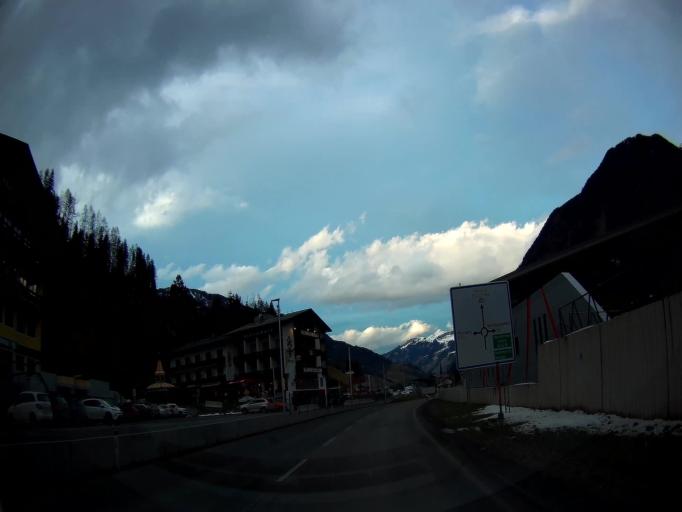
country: AT
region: Salzburg
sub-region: Politischer Bezirk Sankt Johann im Pongau
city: Bad Hofgastein
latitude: 47.1679
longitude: 13.0977
